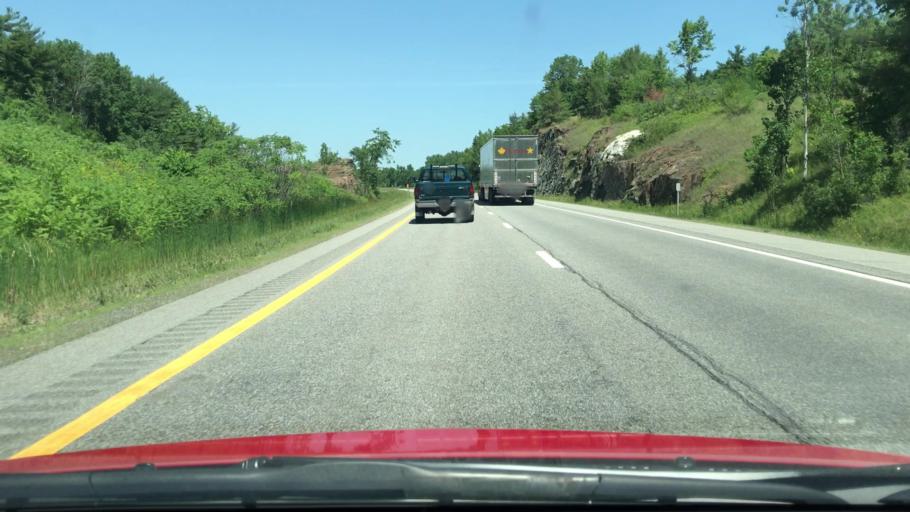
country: US
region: New York
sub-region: Essex County
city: Keeseville
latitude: 44.4286
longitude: -73.4915
